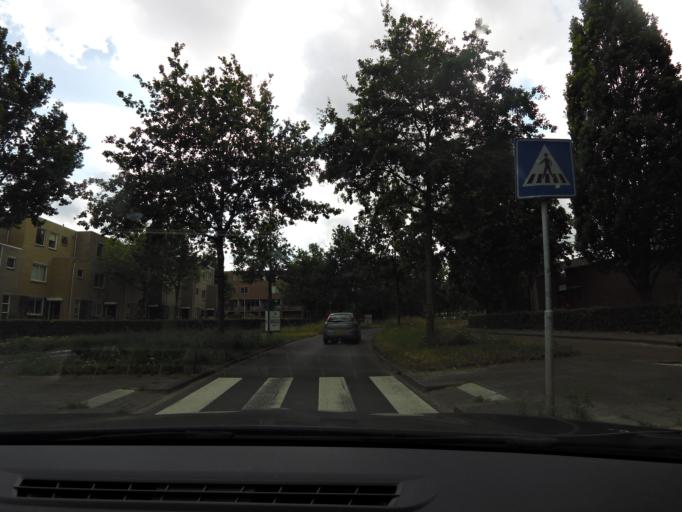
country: NL
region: South Holland
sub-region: Gemeente Vlaardingen
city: Vlaardingen
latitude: 51.9335
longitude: 4.3443
